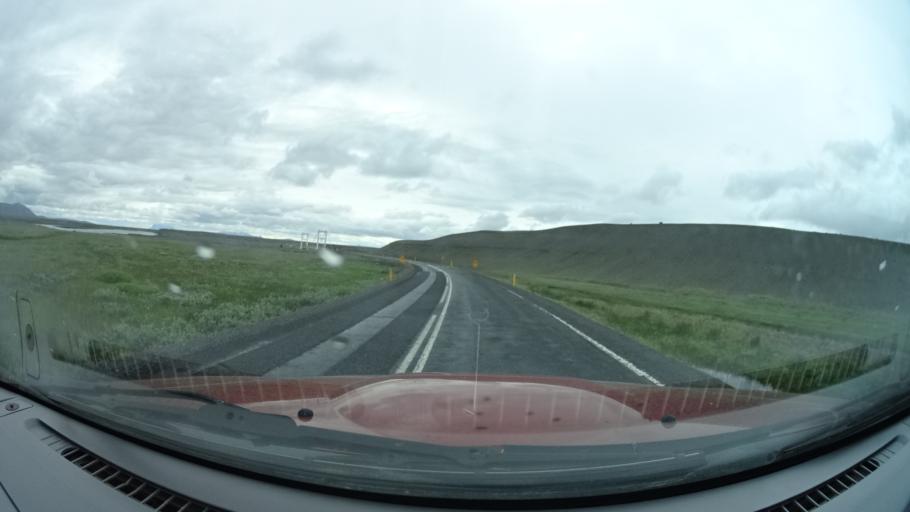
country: IS
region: Northeast
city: Laugar
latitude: 65.6258
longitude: -16.1865
